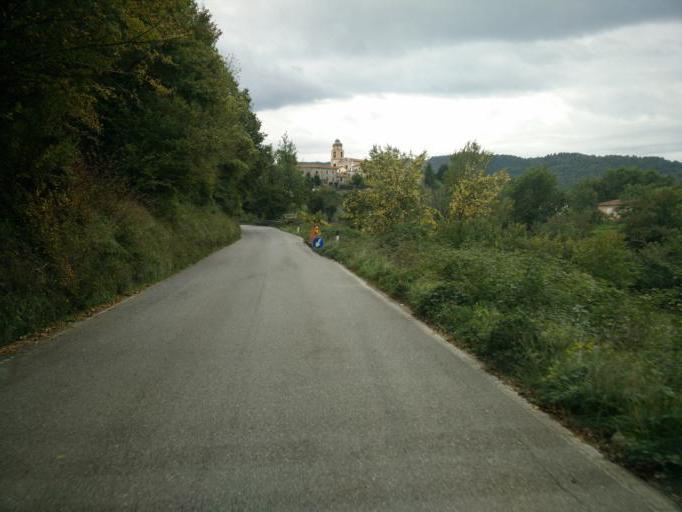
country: IT
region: Tuscany
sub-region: Provincia di Massa-Carrara
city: Fivizzano
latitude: 44.2065
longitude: 10.0931
